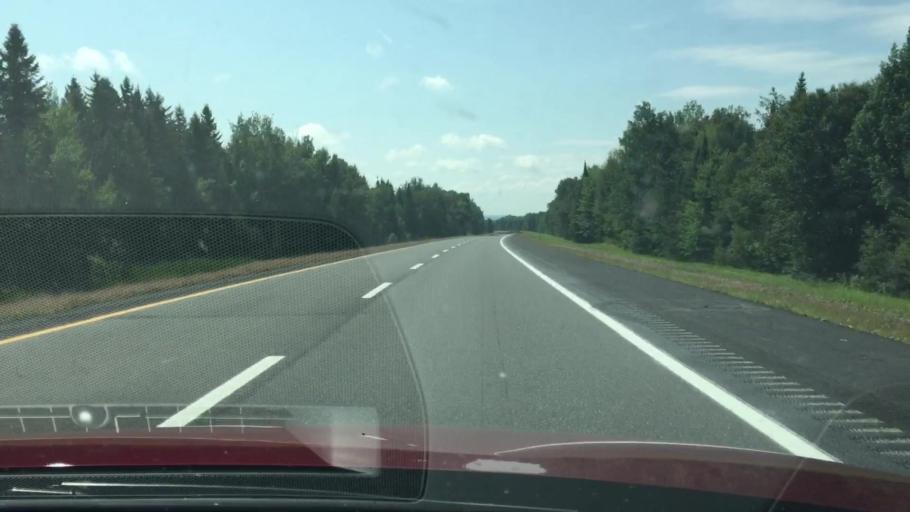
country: US
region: Maine
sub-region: Penobscot County
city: Patten
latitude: 45.9369
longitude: -68.3524
